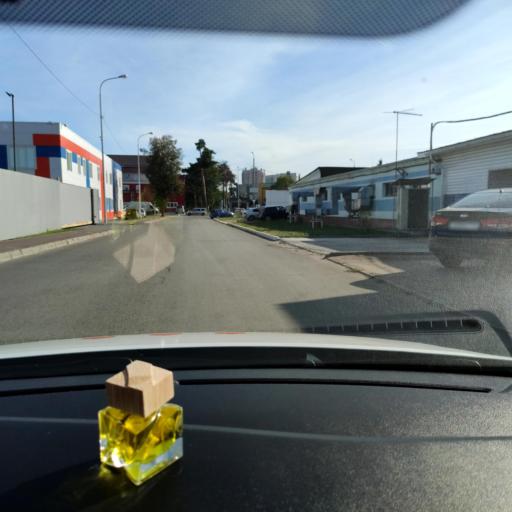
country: RU
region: Tatarstan
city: Staroye Arakchino
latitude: 55.8357
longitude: 49.0499
